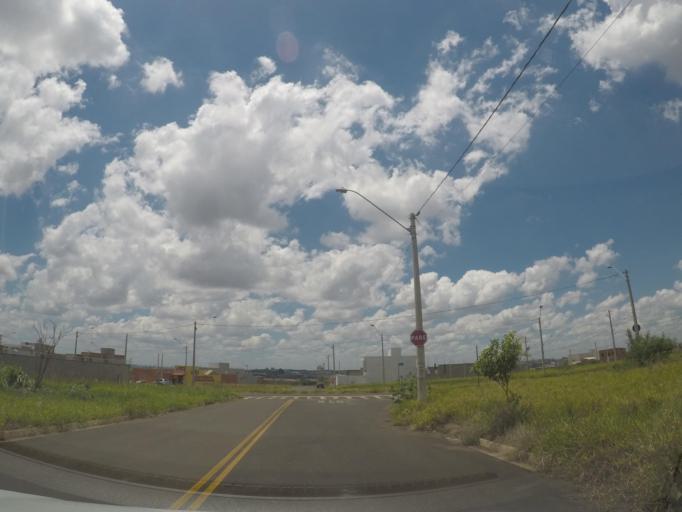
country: BR
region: Sao Paulo
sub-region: Hortolandia
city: Hortolandia
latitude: -22.8390
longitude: -47.2261
